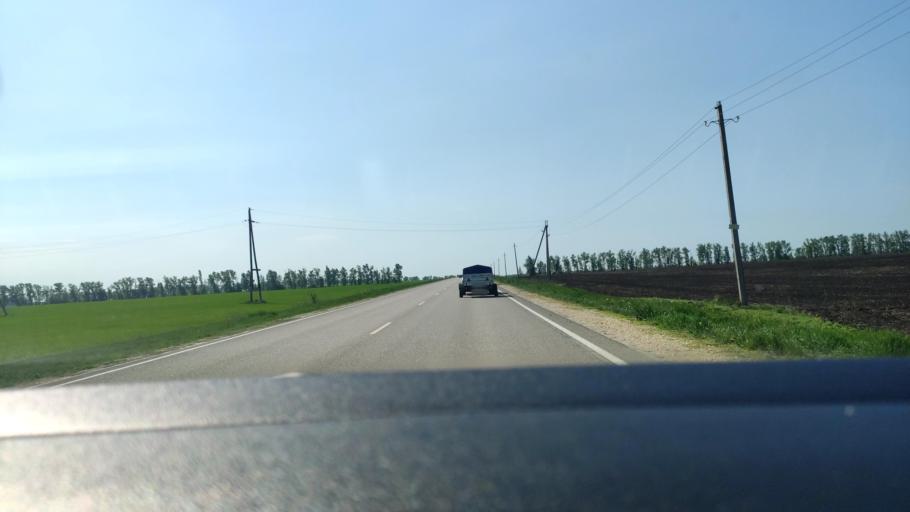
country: RU
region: Voronezj
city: Novaya Usman'
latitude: 51.5701
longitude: 39.3754
